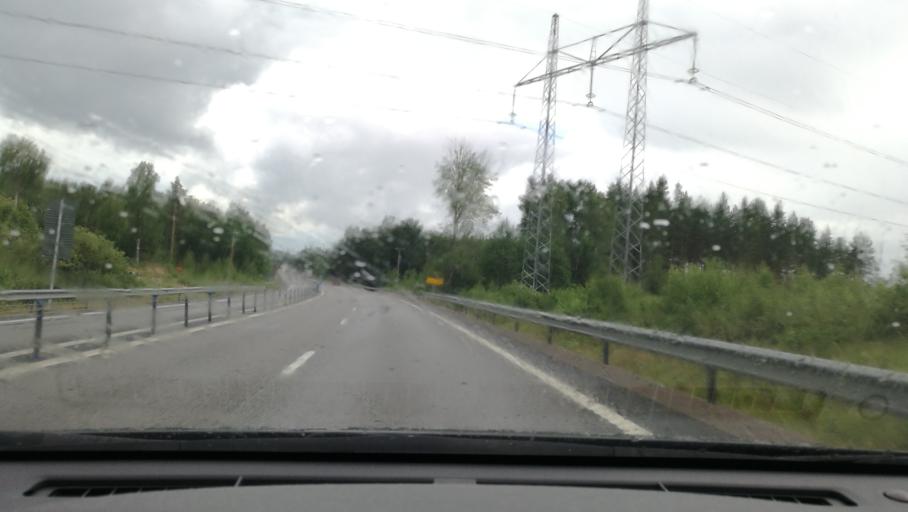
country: SE
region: OEstergoetland
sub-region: Norrkopings Kommun
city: Jursla
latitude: 58.8066
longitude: 16.1514
